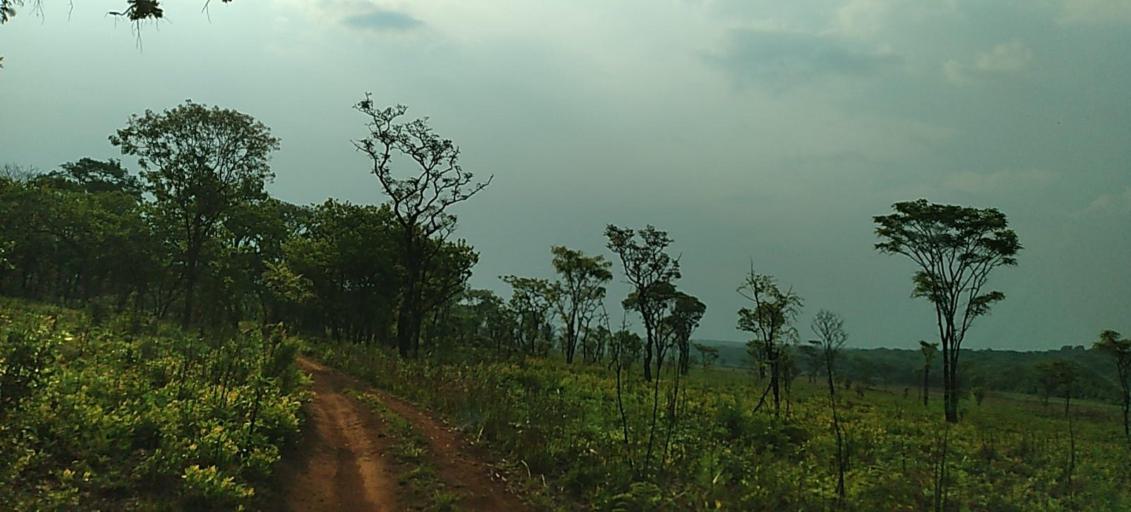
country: ZM
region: North-Western
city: Solwezi
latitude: -12.0434
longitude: 26.0525
